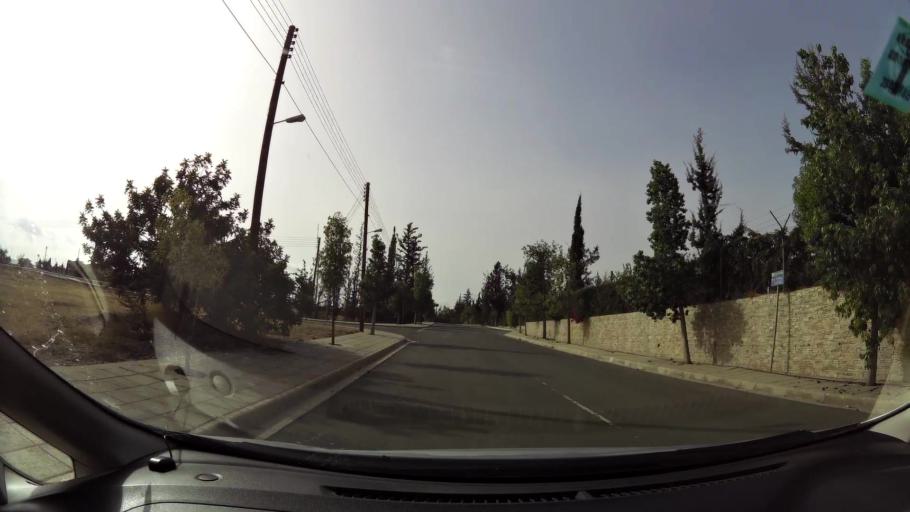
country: CY
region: Lefkosia
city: Geri
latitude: 35.0766
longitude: 33.3840
